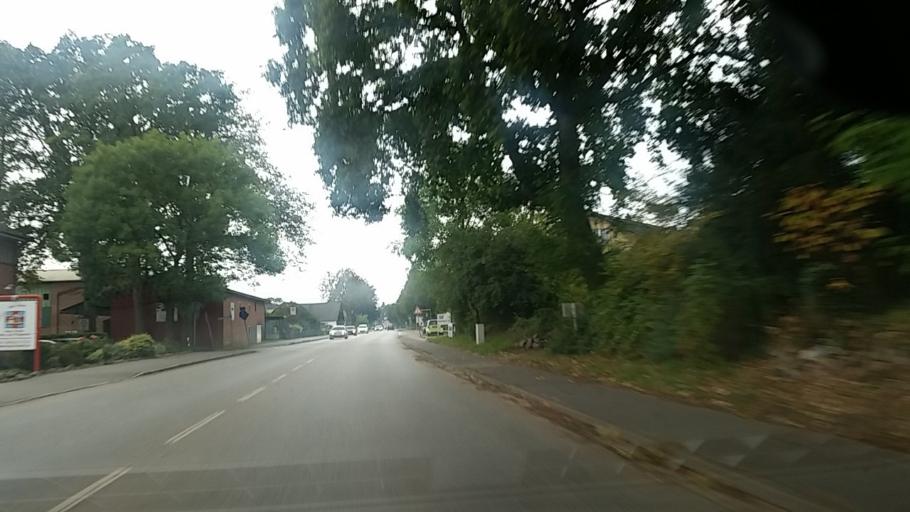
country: DE
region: Schleswig-Holstein
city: Itzstedt
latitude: 53.8107
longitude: 10.1634
